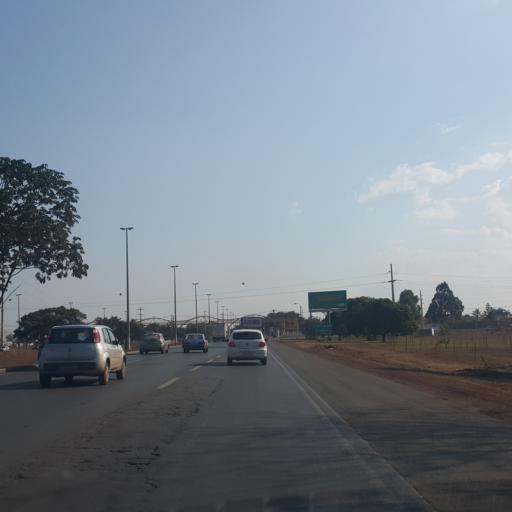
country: BR
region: Federal District
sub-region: Brasilia
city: Brasilia
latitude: -15.8766
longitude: -48.0498
